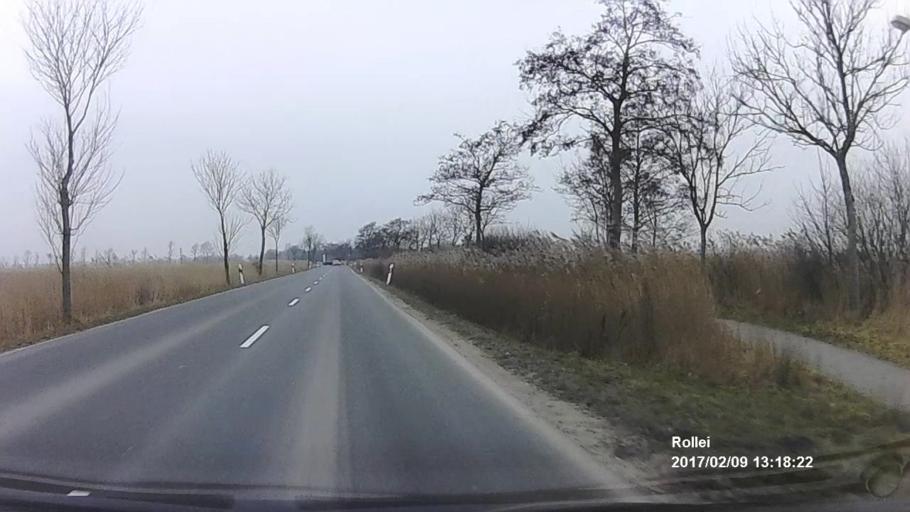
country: DE
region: Lower Saxony
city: Hinte
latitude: 53.4284
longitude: 7.1785
